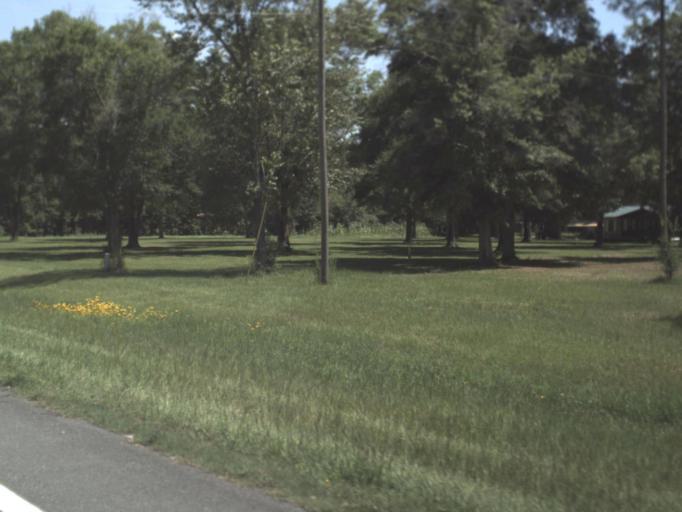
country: US
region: Florida
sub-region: Lafayette County
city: Mayo
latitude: 30.1195
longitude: -83.2630
